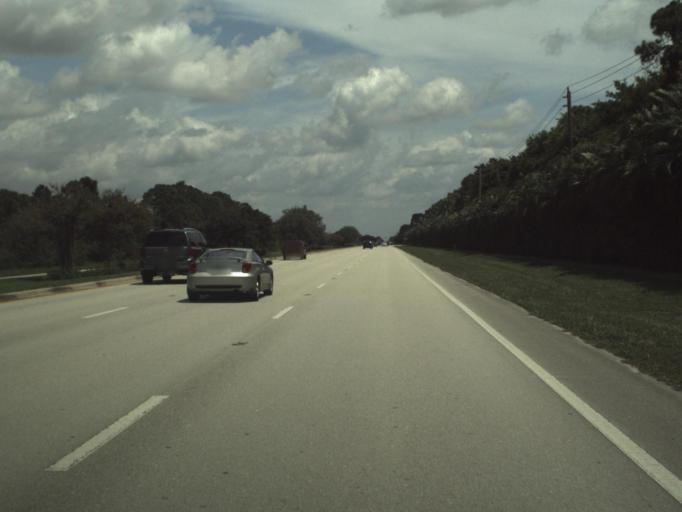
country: US
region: Florida
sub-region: Palm Beach County
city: Juno Beach
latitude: 26.8714
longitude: -80.0955
